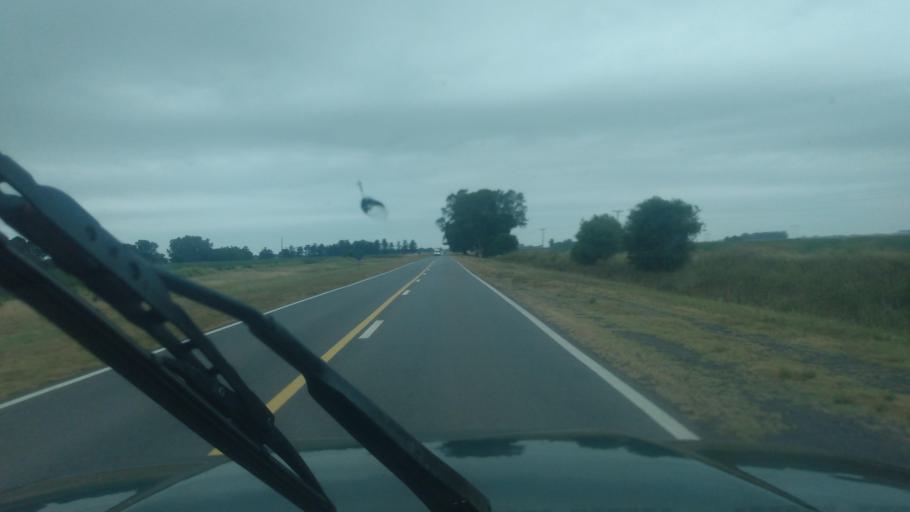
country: AR
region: Buenos Aires
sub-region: Partido de Bragado
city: Bragado
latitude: -35.2750
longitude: -60.5851
